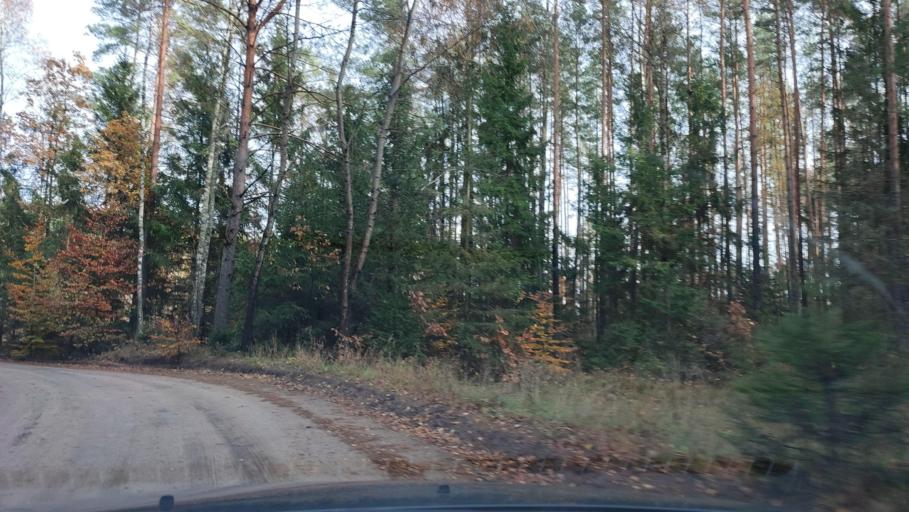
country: PL
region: Warmian-Masurian Voivodeship
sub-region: Powiat szczycienski
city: Szczytno
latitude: 53.5247
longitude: 20.9065
